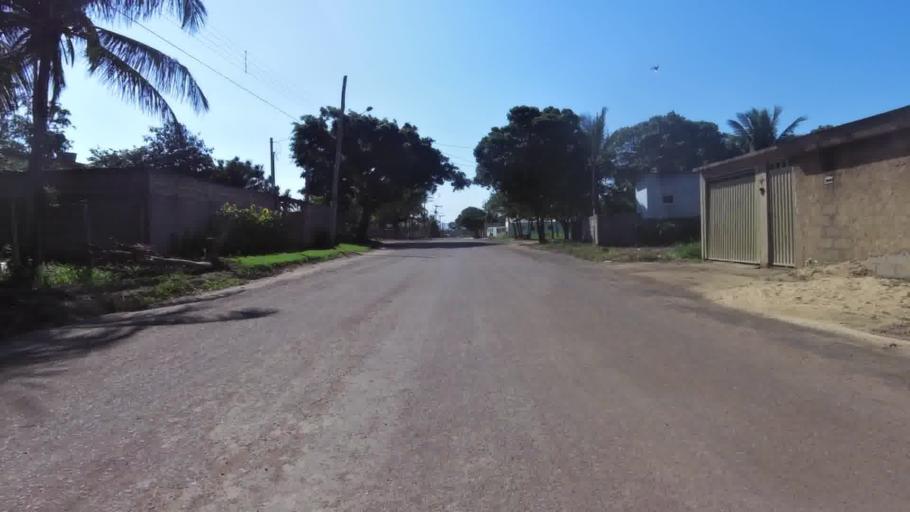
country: BR
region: Espirito Santo
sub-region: Piuma
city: Piuma
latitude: -20.8249
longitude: -40.6208
